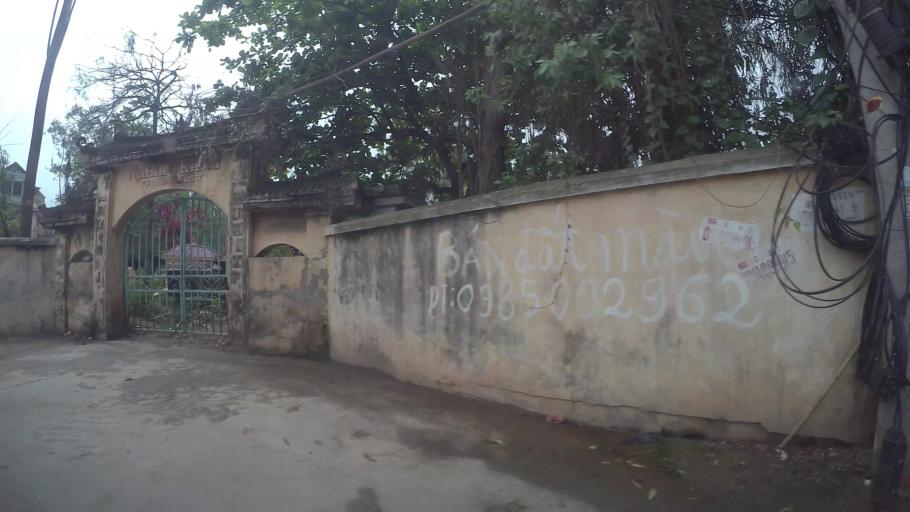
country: VN
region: Ha Noi
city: Van Dien
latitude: 20.9740
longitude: 105.8448
